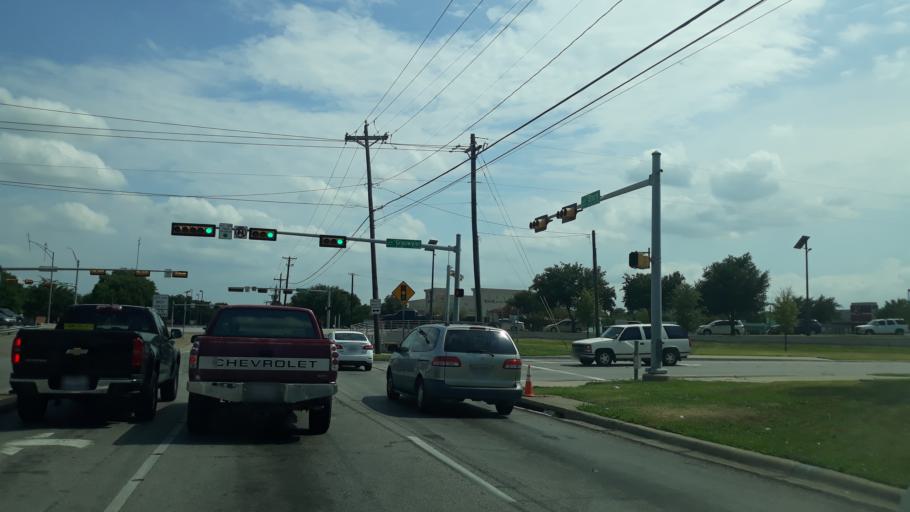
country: US
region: Texas
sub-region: Dallas County
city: Irving
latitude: 32.8293
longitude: -96.9765
